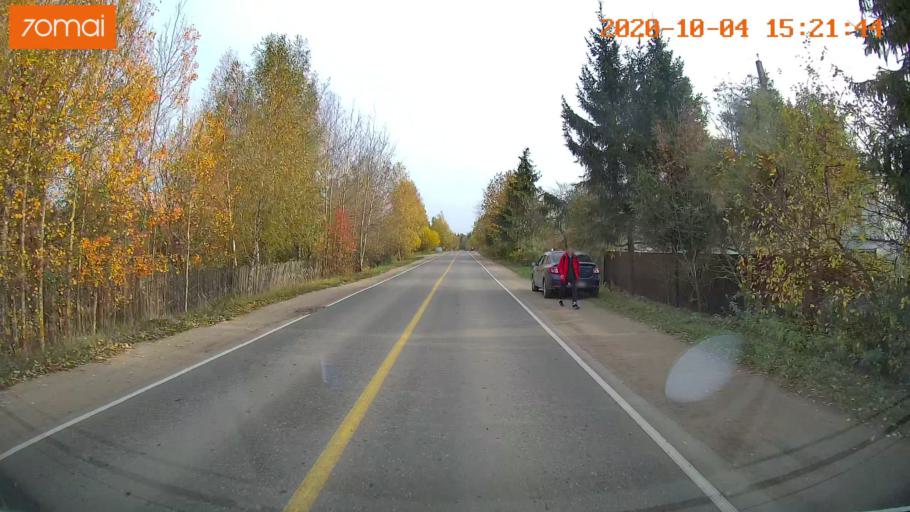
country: RU
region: Ivanovo
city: Bogorodskoye
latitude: 57.0847
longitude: 40.9261
